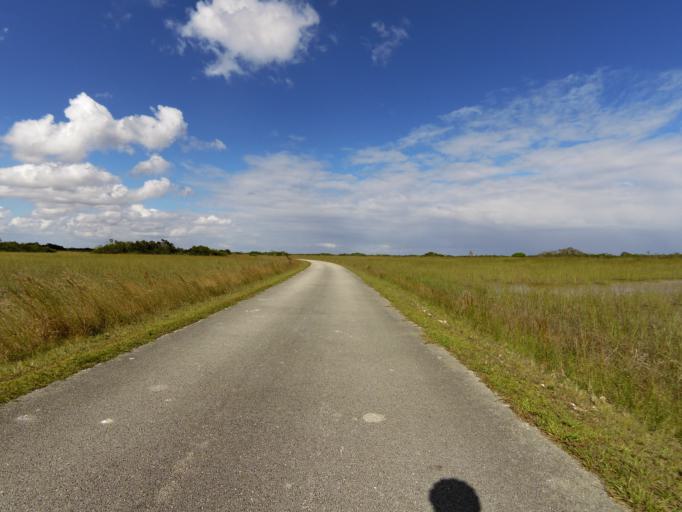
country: US
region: Florida
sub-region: Miami-Dade County
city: The Hammocks
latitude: 25.7367
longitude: -80.7591
